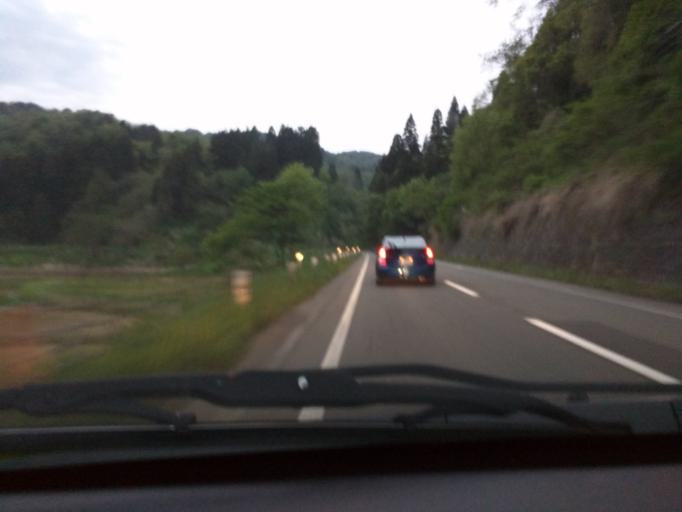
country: JP
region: Niigata
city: Ojiya
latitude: 37.3223
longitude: 138.6848
